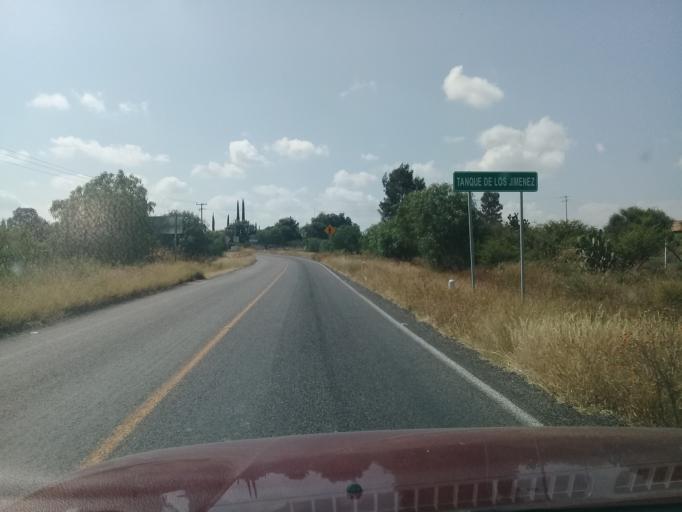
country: MX
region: Aguascalientes
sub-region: Aguascalientes
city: Penuelas (El Cienegal)
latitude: 21.7120
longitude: -102.3732
